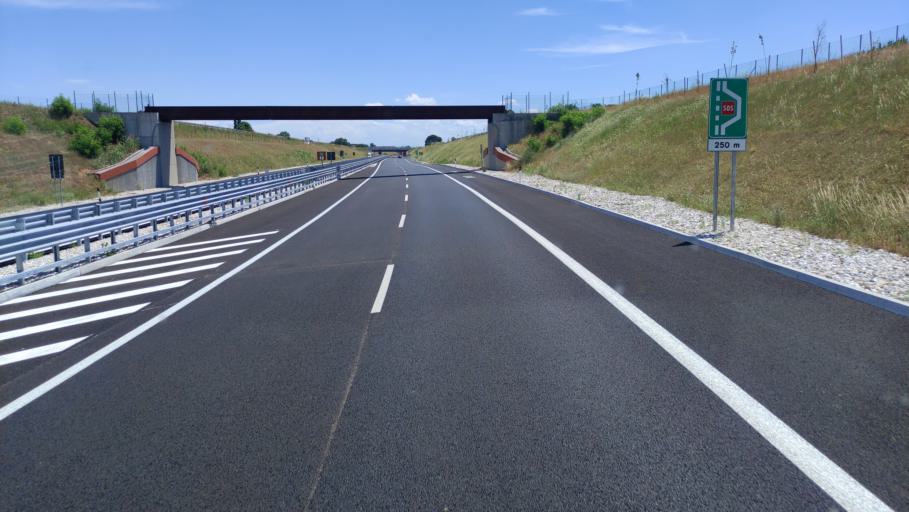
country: IT
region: Veneto
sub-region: Provincia di Treviso
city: San Vito
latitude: 45.7449
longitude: 11.9215
